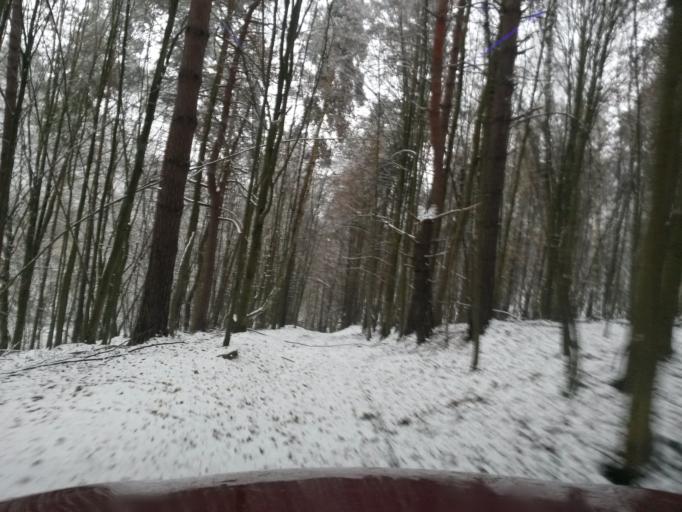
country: SK
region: Presovsky
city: Sabinov
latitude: 48.9879
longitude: 21.0919
